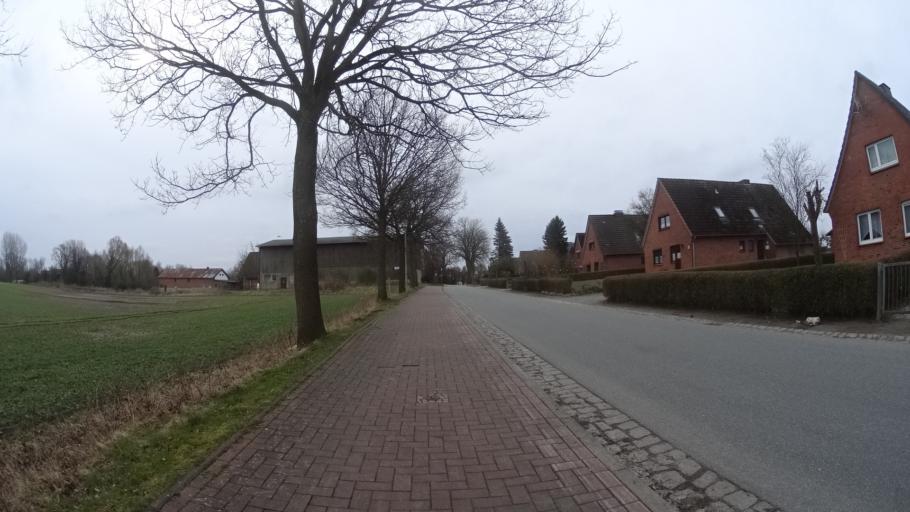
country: DE
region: Schleswig-Holstein
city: Stakendorf
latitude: 54.3916
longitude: 10.4208
